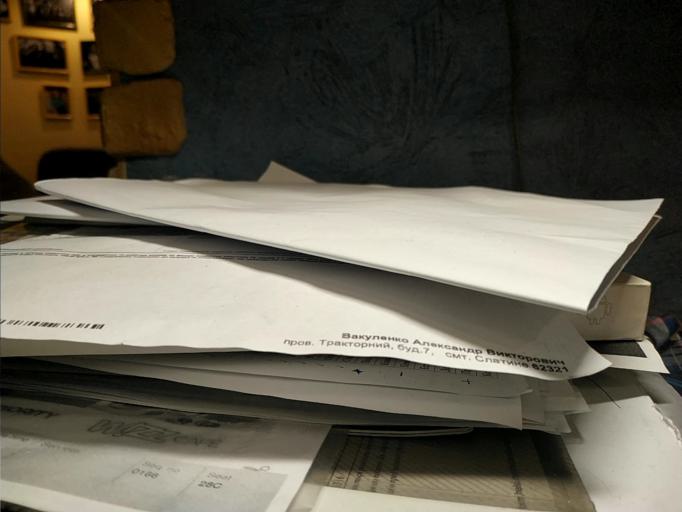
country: RU
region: Tverskaya
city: Zubtsov
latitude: 56.0964
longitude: 34.7094
